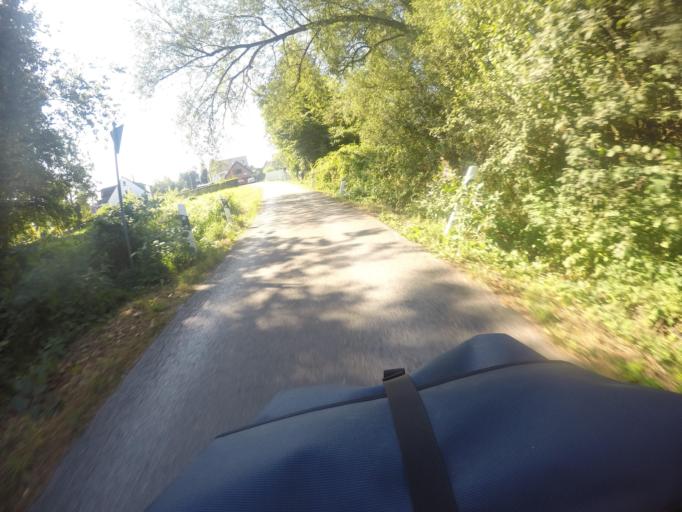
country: DE
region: North Rhine-Westphalia
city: Leichlingen
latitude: 51.1282
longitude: 6.9994
